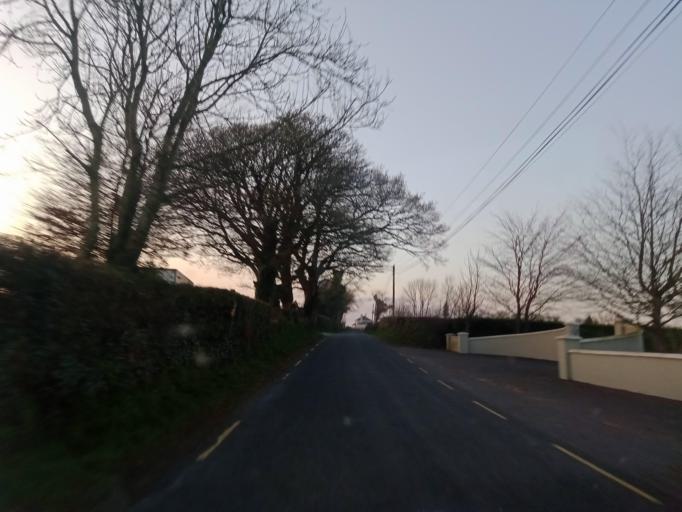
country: IE
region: Leinster
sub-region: Laois
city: Abbeyleix
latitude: 52.9616
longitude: -7.3654
